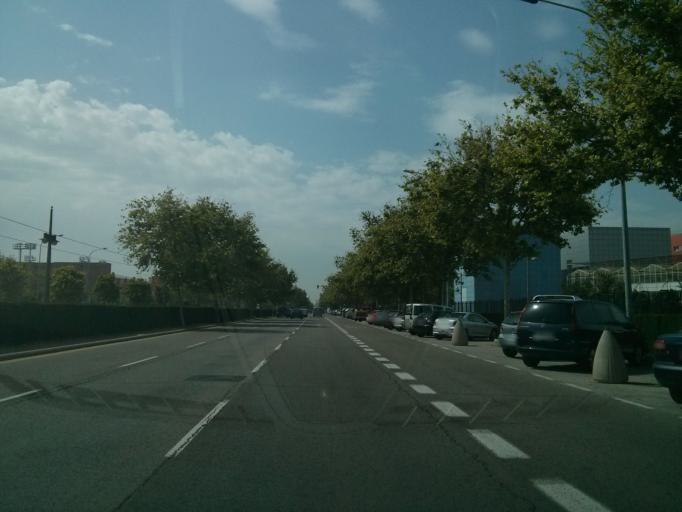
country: ES
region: Valencia
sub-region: Provincia de Valencia
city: Alboraya
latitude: 39.4776
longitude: -0.3369
